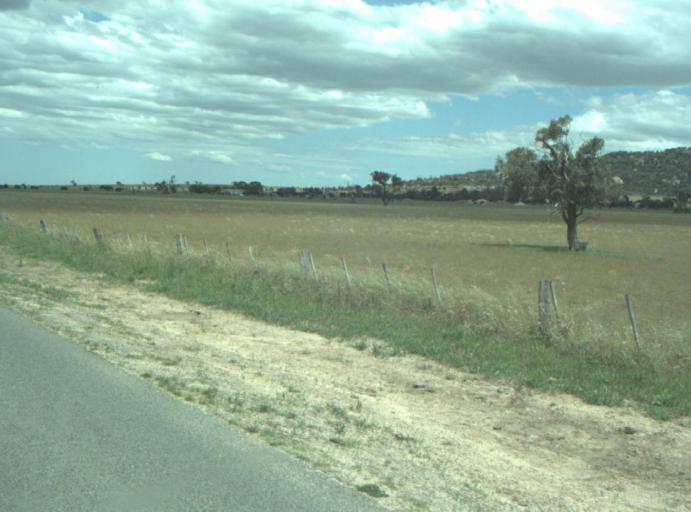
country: AU
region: Victoria
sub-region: Wyndham
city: Little River
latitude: -37.9193
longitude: 144.4633
